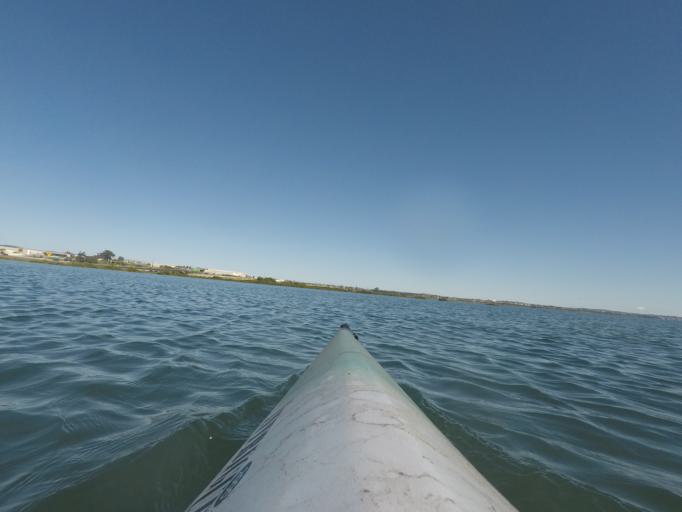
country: NZ
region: Auckland
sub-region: Auckland
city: Rosebank
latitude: -36.8698
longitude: 174.6803
